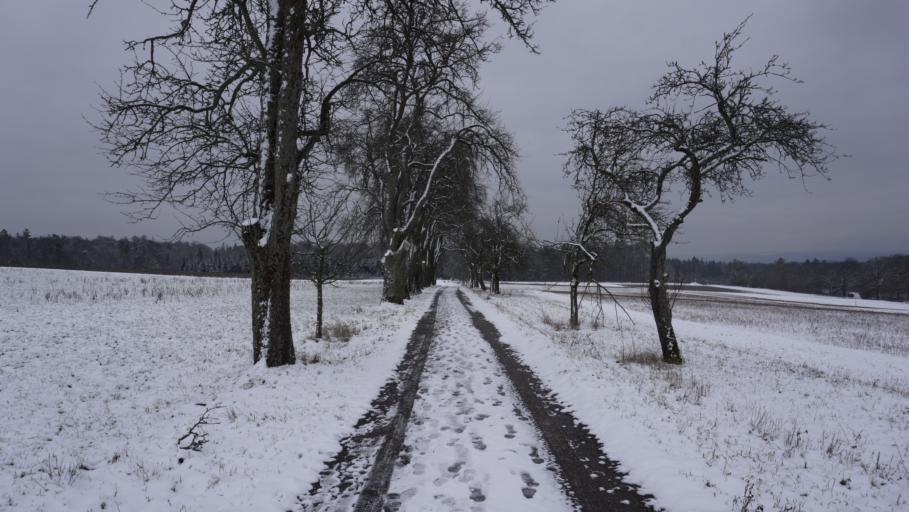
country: DE
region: Baden-Wuerttemberg
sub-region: Karlsruhe Region
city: Neckargerach
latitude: 49.4395
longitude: 9.0982
